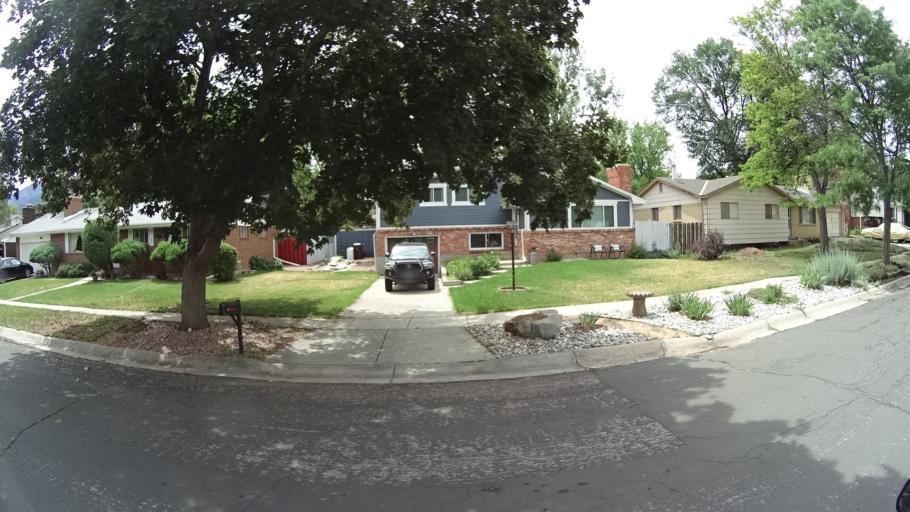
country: US
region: Colorado
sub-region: El Paso County
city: Manitou Springs
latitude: 38.8681
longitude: -104.8695
